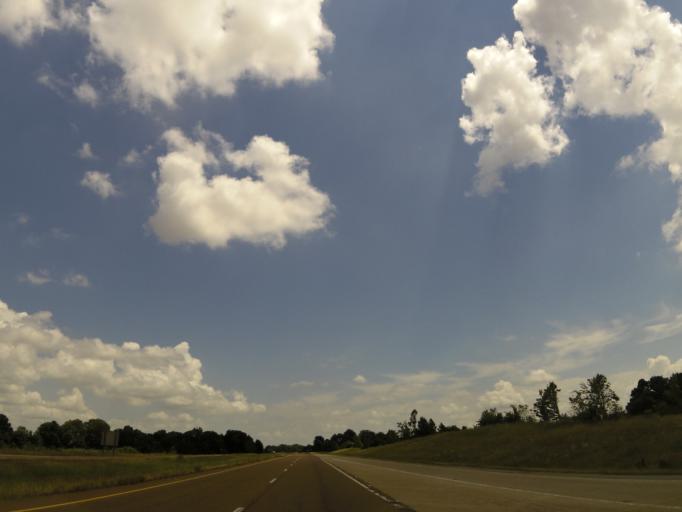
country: US
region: Tennessee
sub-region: Dyer County
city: Dyersburg
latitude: 35.9631
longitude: -89.3289
